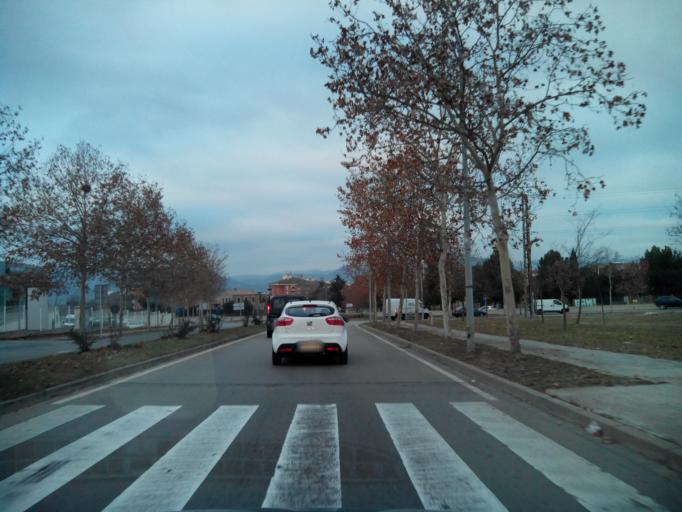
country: ES
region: Catalonia
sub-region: Provincia de Barcelona
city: Manresa
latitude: 41.7171
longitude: 1.8462
